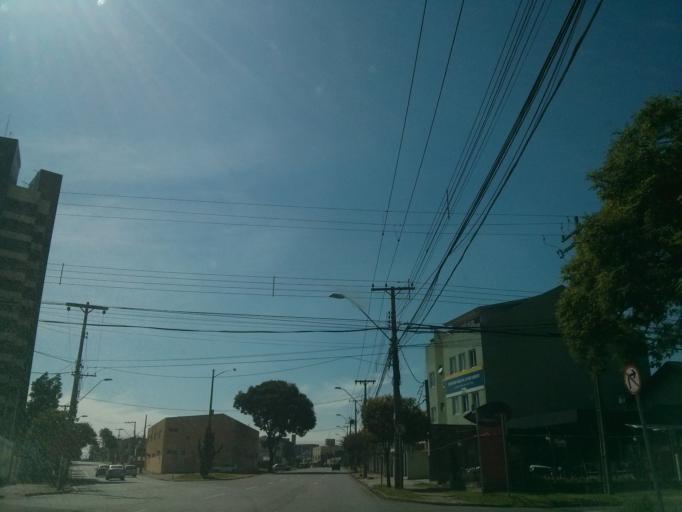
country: BR
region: Parana
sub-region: Sao Jose Dos Pinhais
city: Sao Jose dos Pinhais
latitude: -25.5332
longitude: -49.2112
